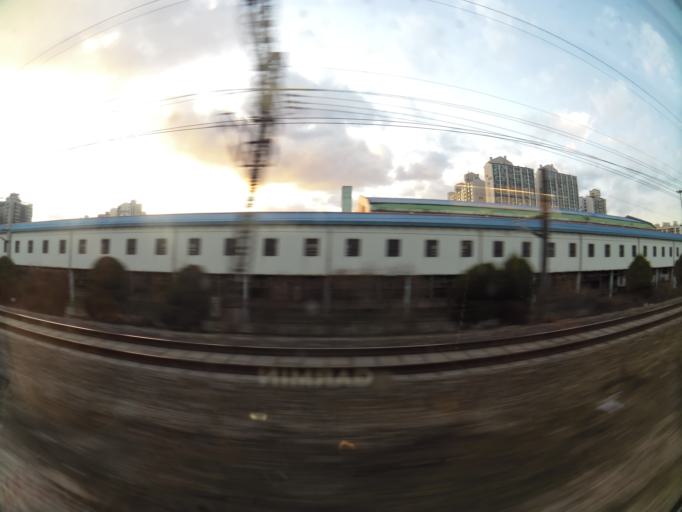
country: KR
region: Gyeonggi-do
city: Kwangmyong
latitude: 37.4887
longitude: 126.8798
